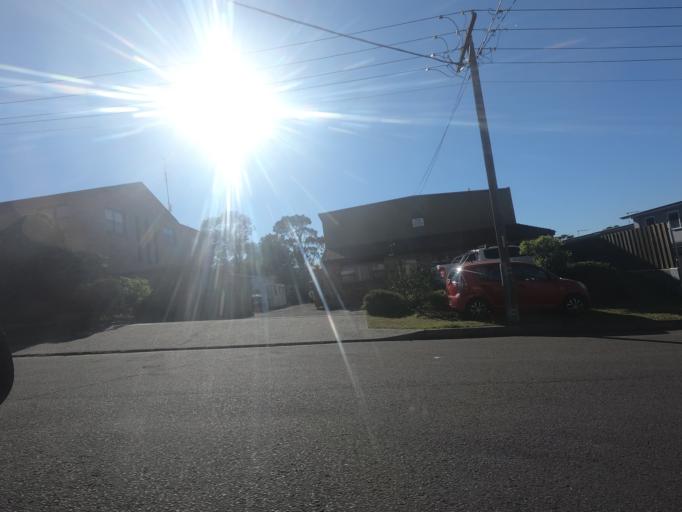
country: AU
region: New South Wales
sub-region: Wollongong
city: Corrimal
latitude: -34.3730
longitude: 150.8881
